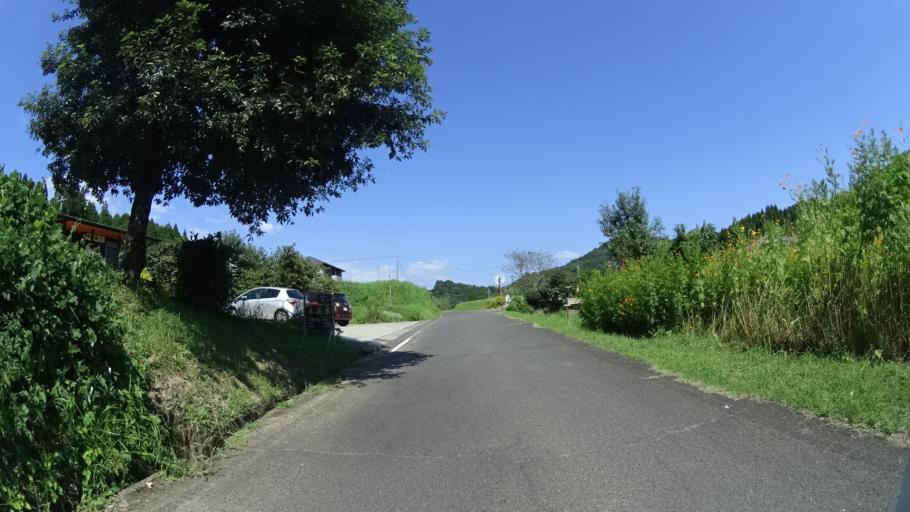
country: JP
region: Kagoshima
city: Kajiki
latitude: 31.7544
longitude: 130.6730
